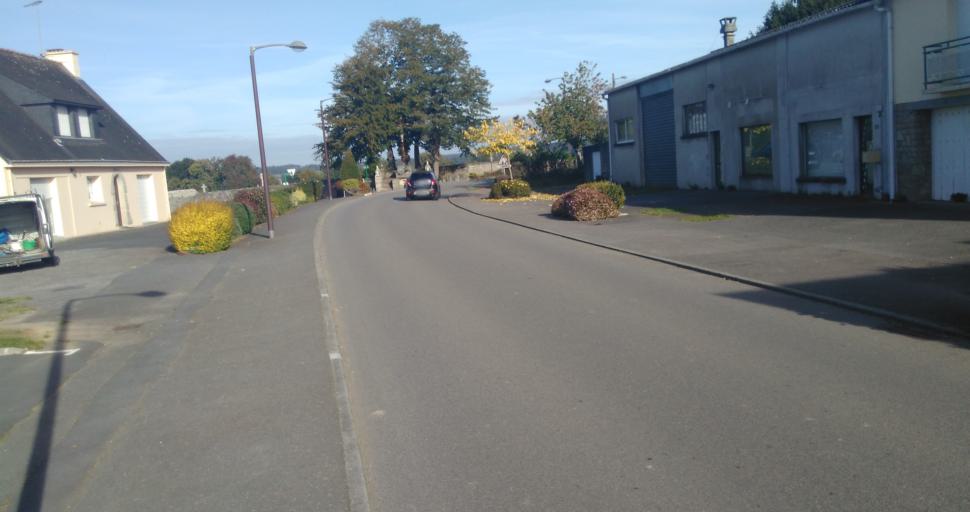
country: FR
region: Brittany
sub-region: Departement du Morbihan
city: Peillac
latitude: 47.7408
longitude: -2.2136
